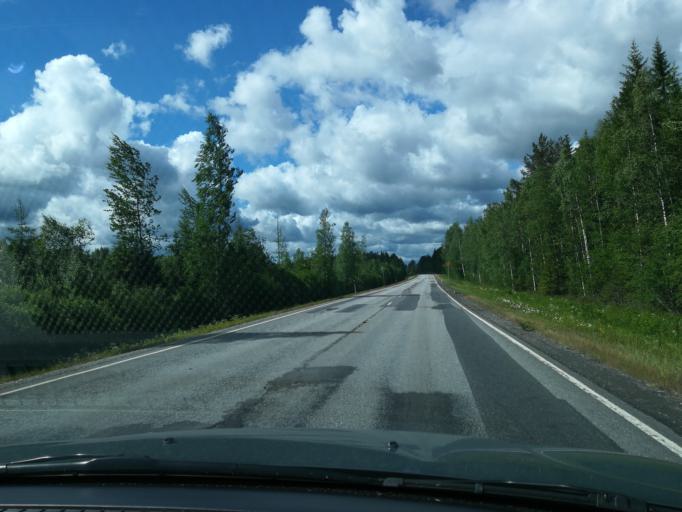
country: FI
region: Southern Savonia
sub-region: Mikkeli
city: Ristiina
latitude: 61.4322
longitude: 27.2383
